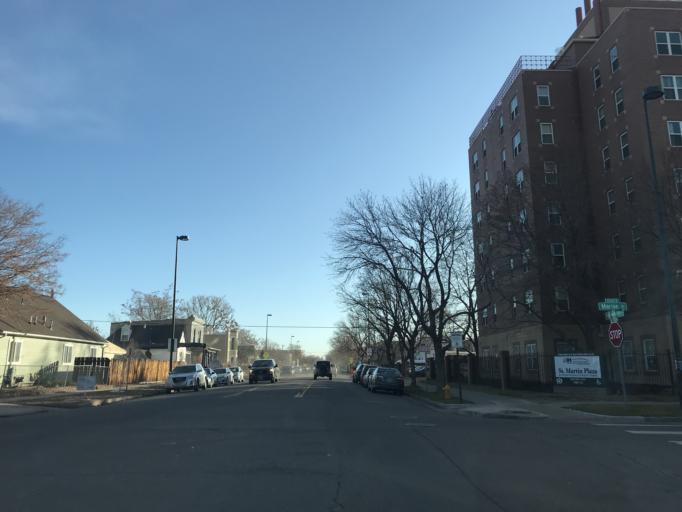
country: US
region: Colorado
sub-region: Denver County
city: Denver
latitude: 39.7645
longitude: -104.9723
